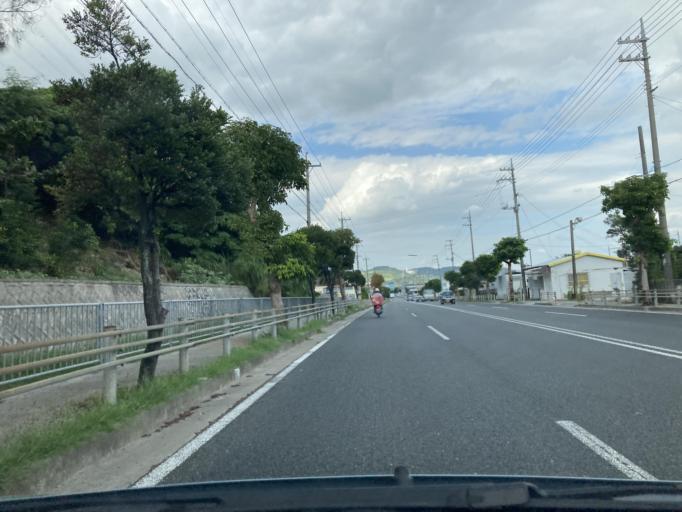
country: JP
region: Okinawa
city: Ginowan
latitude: 26.2510
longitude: 127.7829
